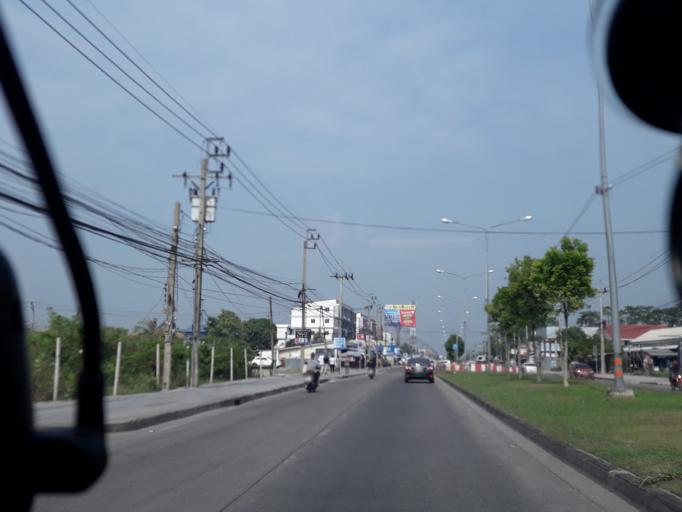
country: TH
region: Bangkok
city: Khlong Sam Wa
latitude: 13.8355
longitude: 100.7200
